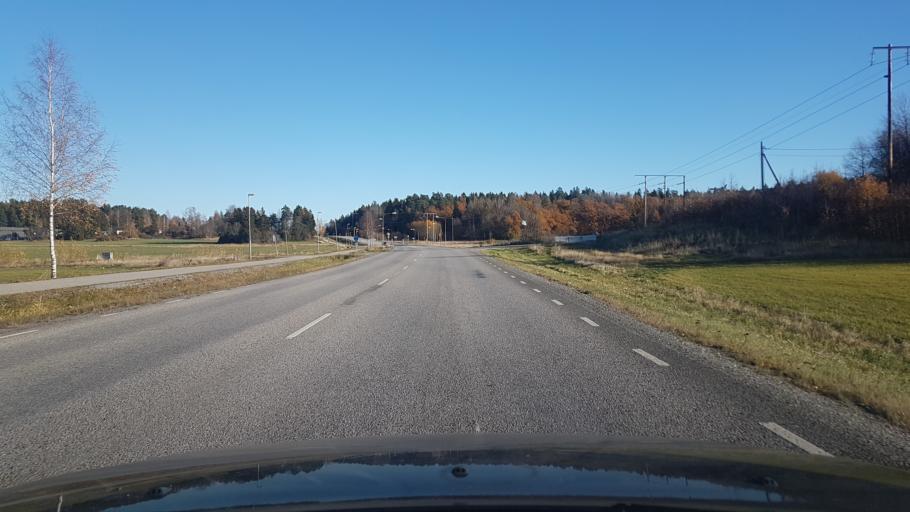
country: SE
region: Stockholm
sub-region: Sigtuna Kommun
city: Marsta
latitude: 59.6284
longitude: 17.8846
